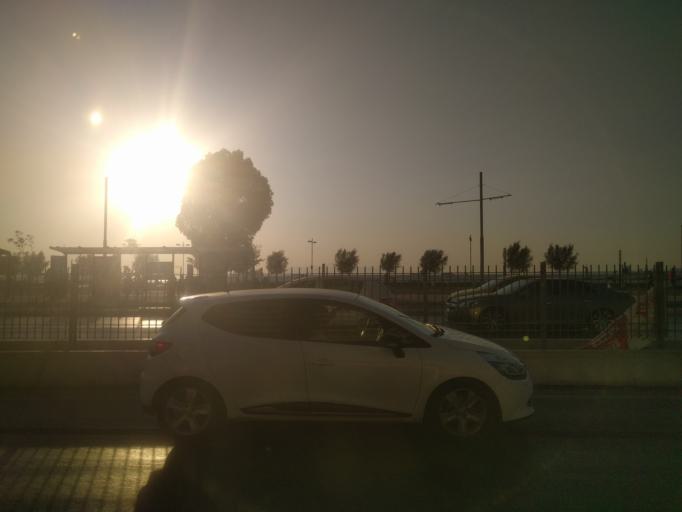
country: TR
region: Izmir
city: Izmir
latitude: 38.4200
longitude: 27.1282
